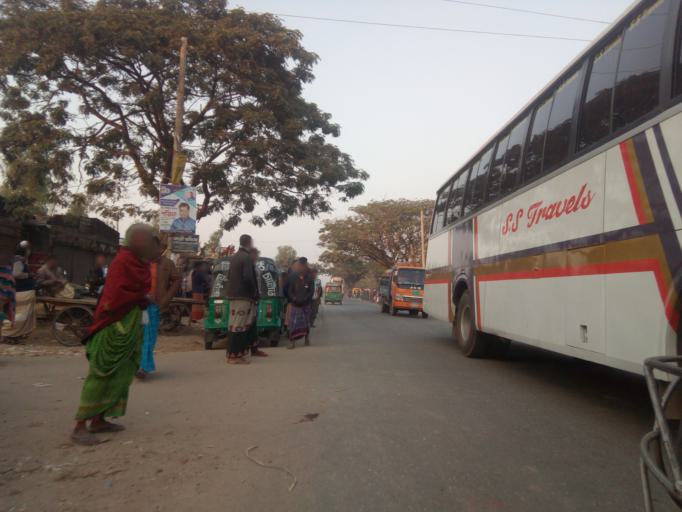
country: BD
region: Rajshahi
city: Bogra
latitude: 24.5931
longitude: 89.2365
